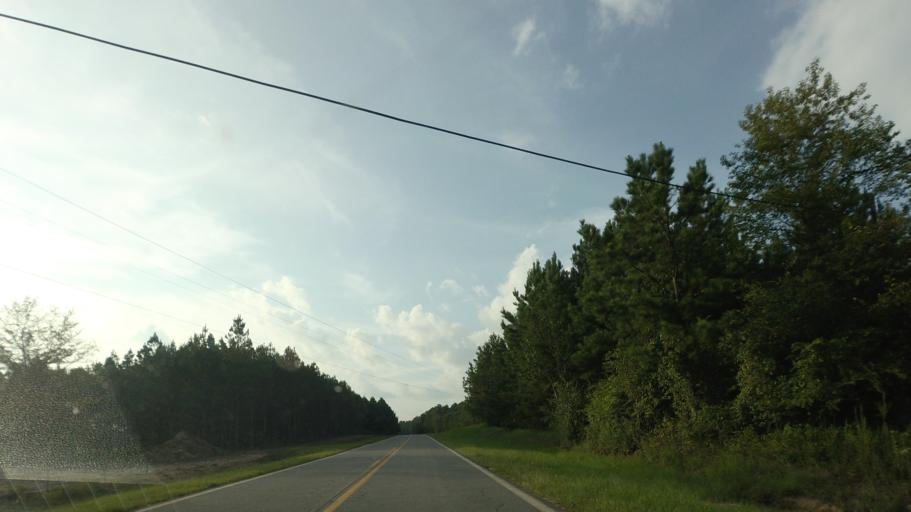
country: US
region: Georgia
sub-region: Wilkinson County
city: Gordon
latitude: 32.8189
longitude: -83.4017
